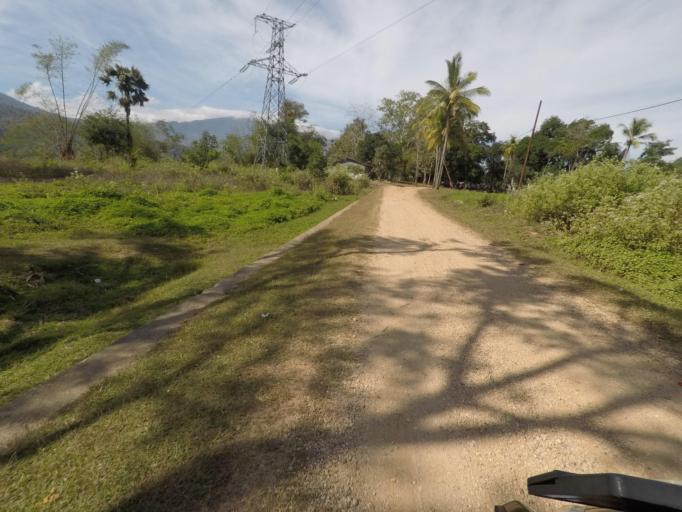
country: TL
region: Bobonaro
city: Maliana
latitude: -8.9591
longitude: 125.2184
